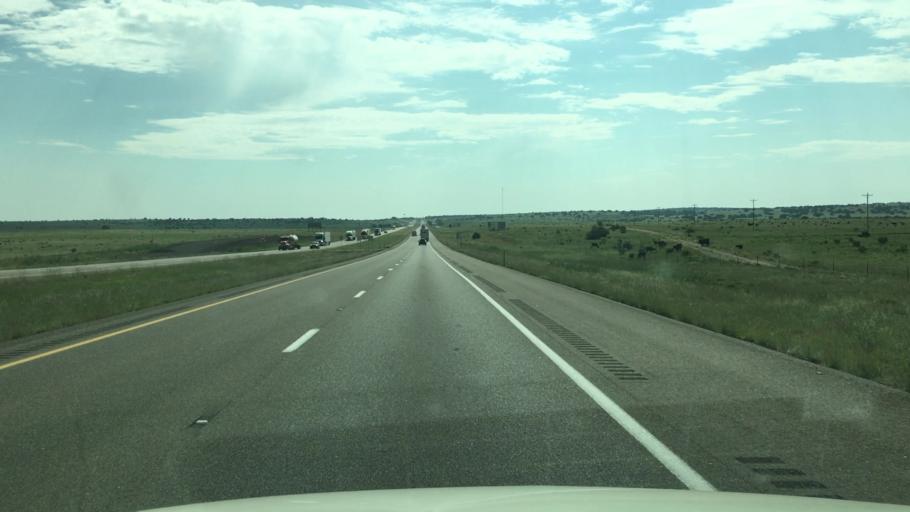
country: US
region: New Mexico
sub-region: Guadalupe County
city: Santa Rosa
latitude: 34.9893
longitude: -105.2517
